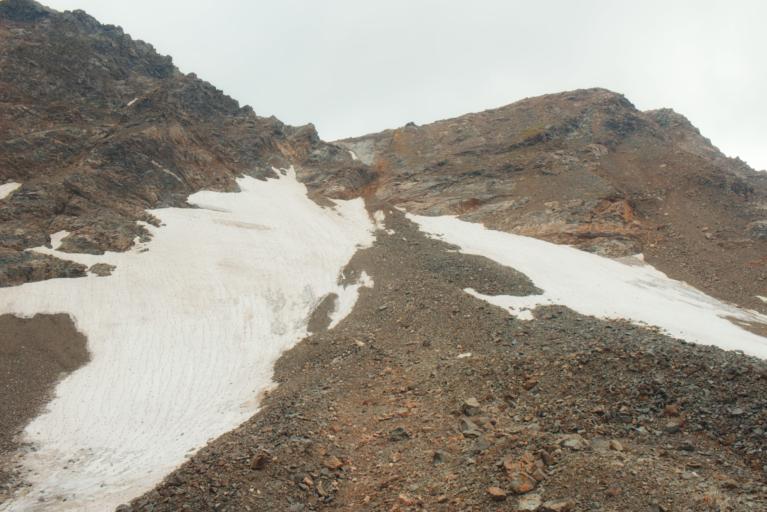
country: RU
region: Karachayevo-Cherkesiya
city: Nizhniy Arkhyz
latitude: 43.4236
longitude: 41.2507
